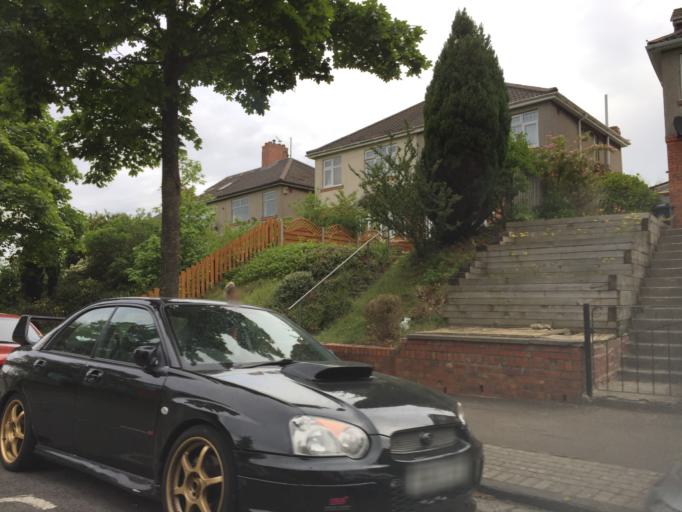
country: GB
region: England
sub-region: Bristol
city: Bristol
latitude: 51.4989
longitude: -2.5901
